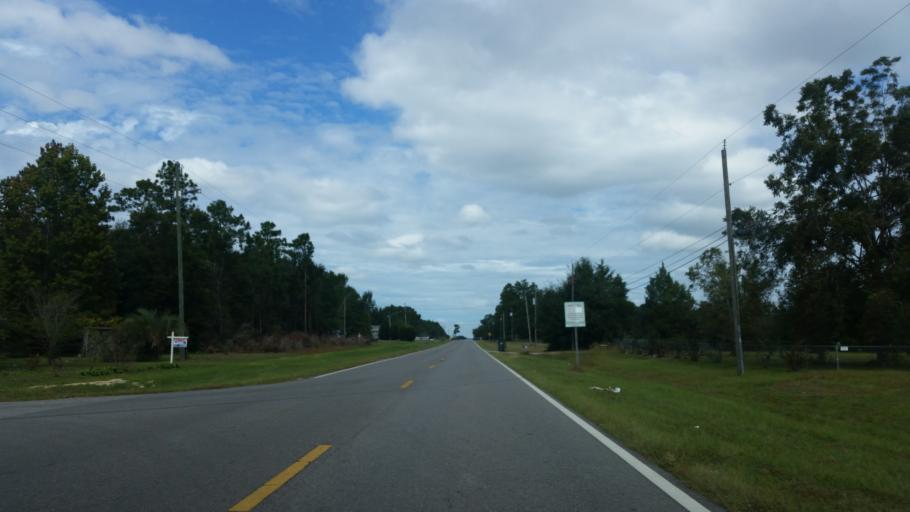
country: US
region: Florida
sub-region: Santa Rosa County
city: Point Baker
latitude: 30.6840
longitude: -86.9936
